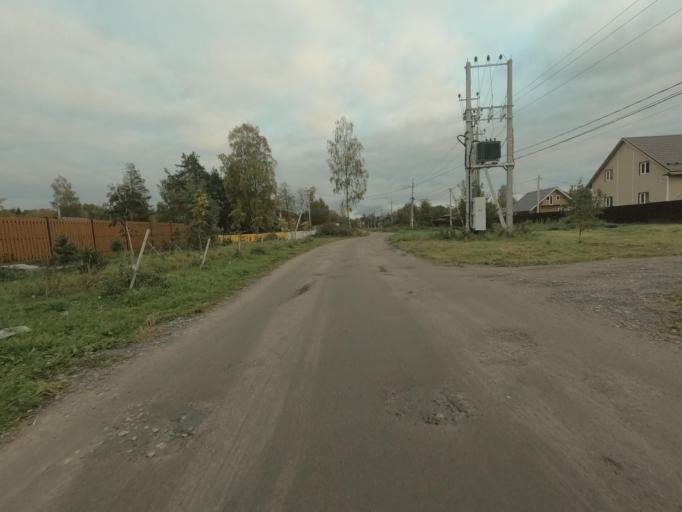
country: RU
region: Leningrad
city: Pavlovo
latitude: 59.8103
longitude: 30.9190
